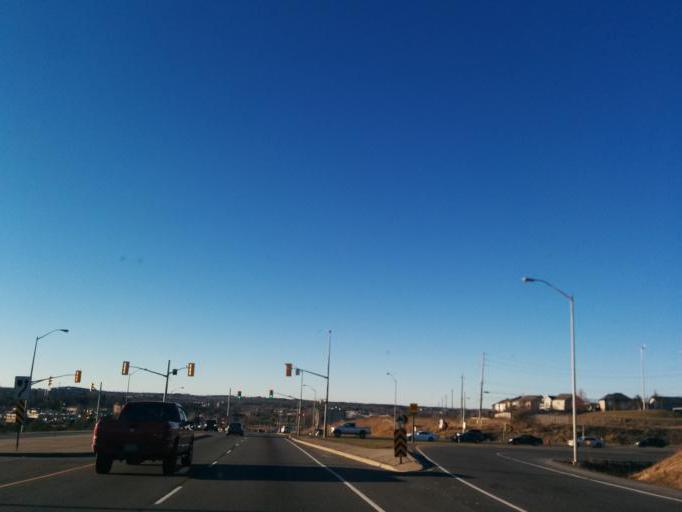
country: CA
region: Ontario
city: Orangeville
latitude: 43.9190
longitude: -80.0763
